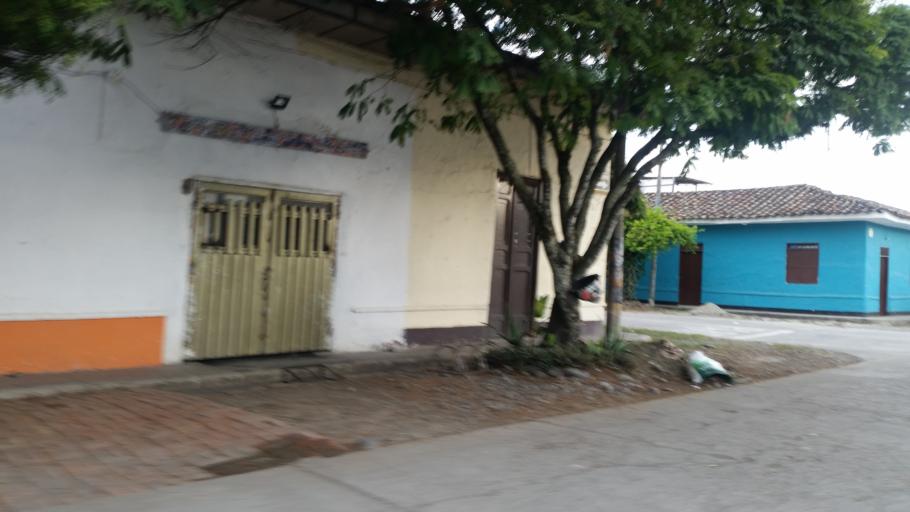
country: CO
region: Valle del Cauca
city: Ginebra
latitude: 3.7248
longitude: -76.2665
